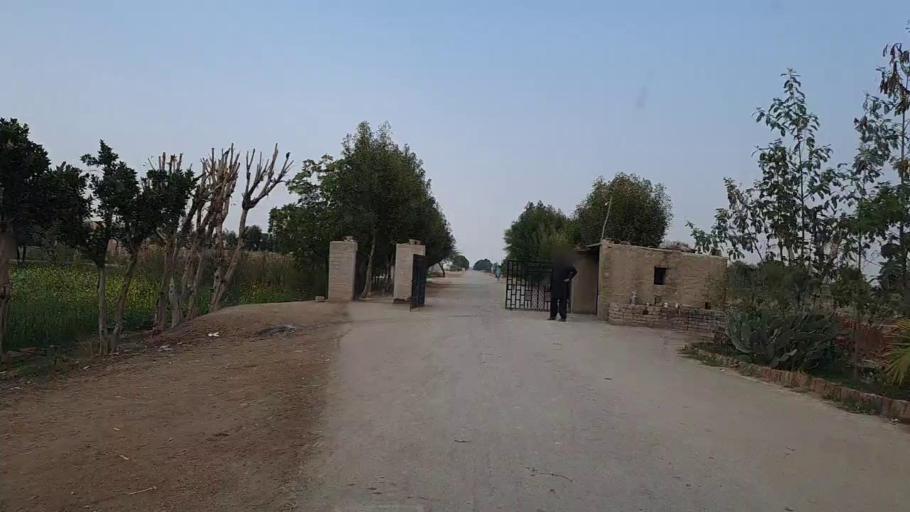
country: PK
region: Sindh
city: Mirwah Gorchani
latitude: 25.3711
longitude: 69.0817
